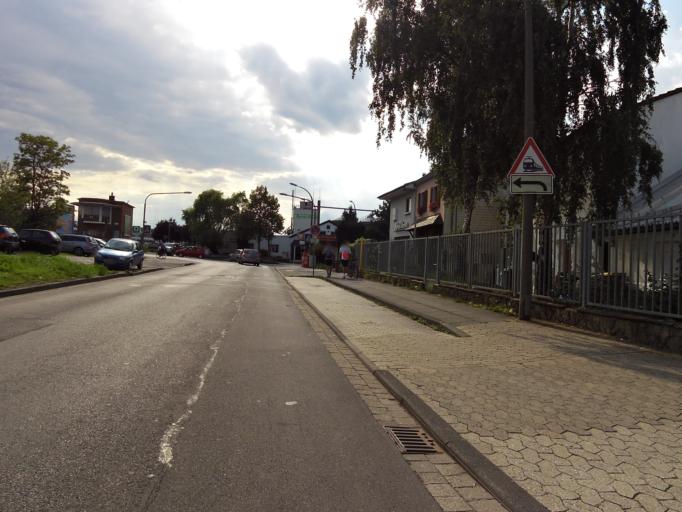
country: DE
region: North Rhine-Westphalia
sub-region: Regierungsbezirk Koln
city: Rheinbach
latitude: 50.6292
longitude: 6.9451
